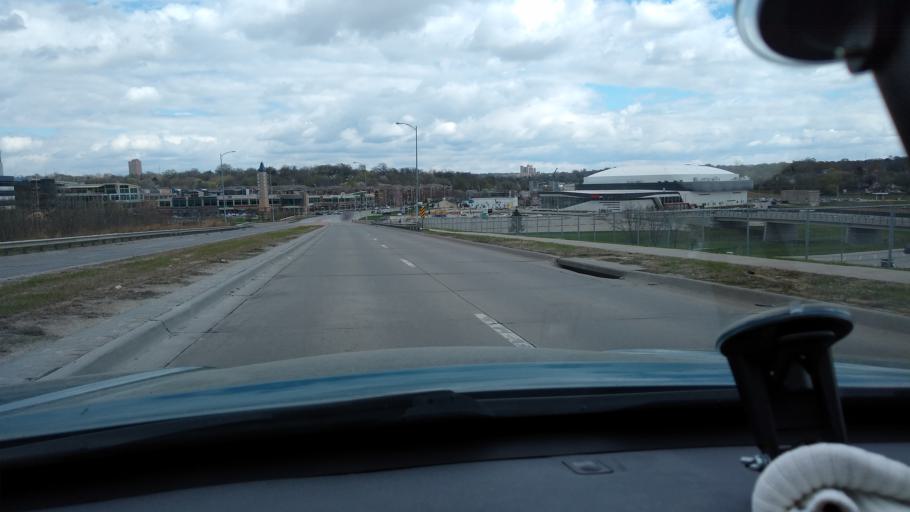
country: US
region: Nebraska
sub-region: Douglas County
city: Ralston
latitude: 41.2361
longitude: -96.0188
